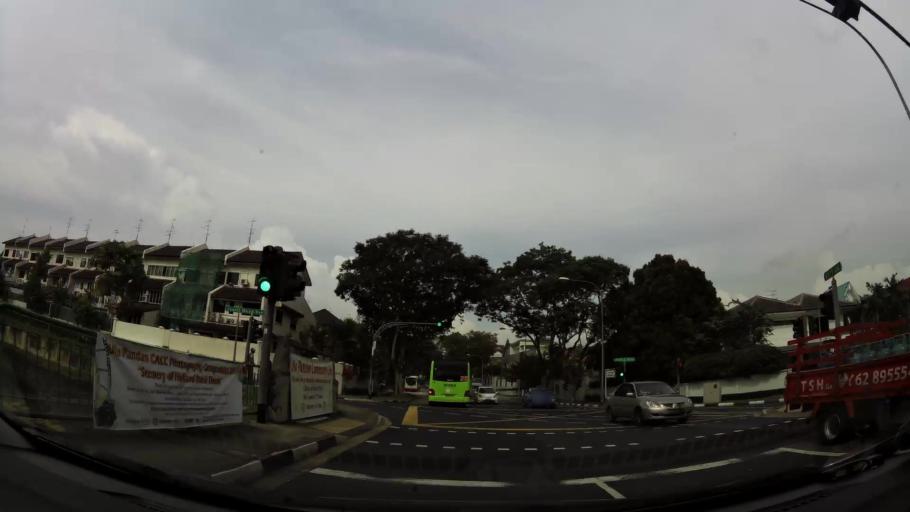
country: SG
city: Singapore
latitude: 1.3249
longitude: 103.7925
